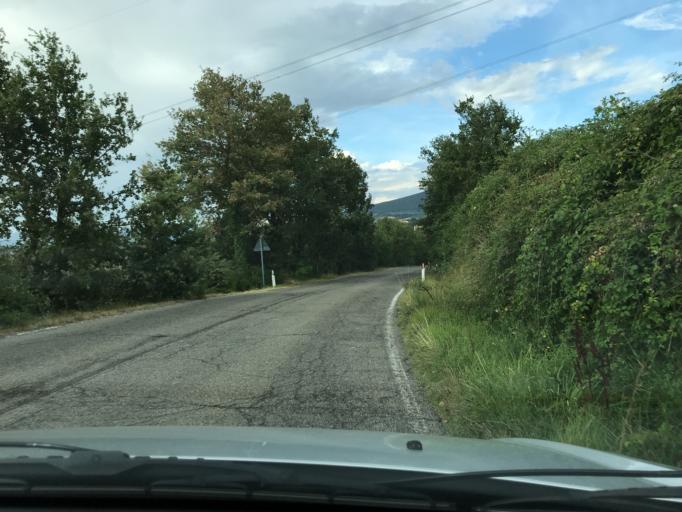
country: IT
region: Umbria
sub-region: Provincia di Terni
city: Montecchio
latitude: 42.6496
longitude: 12.2769
